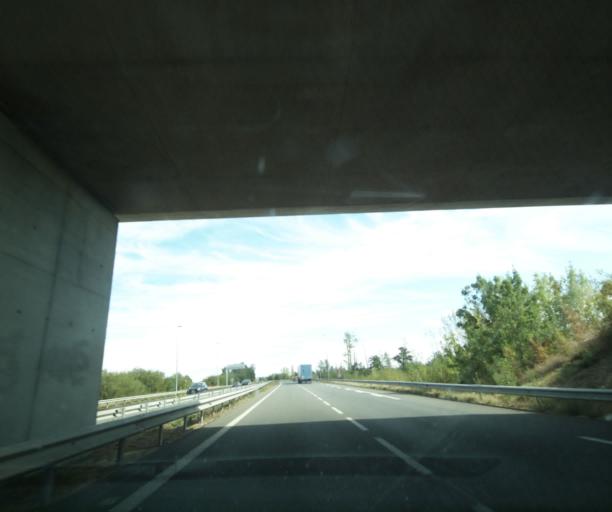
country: FR
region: Midi-Pyrenees
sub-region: Departement du Tarn-et-Garonne
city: Saint-Nicolas-de-la-Grave
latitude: 44.0438
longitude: 0.9984
